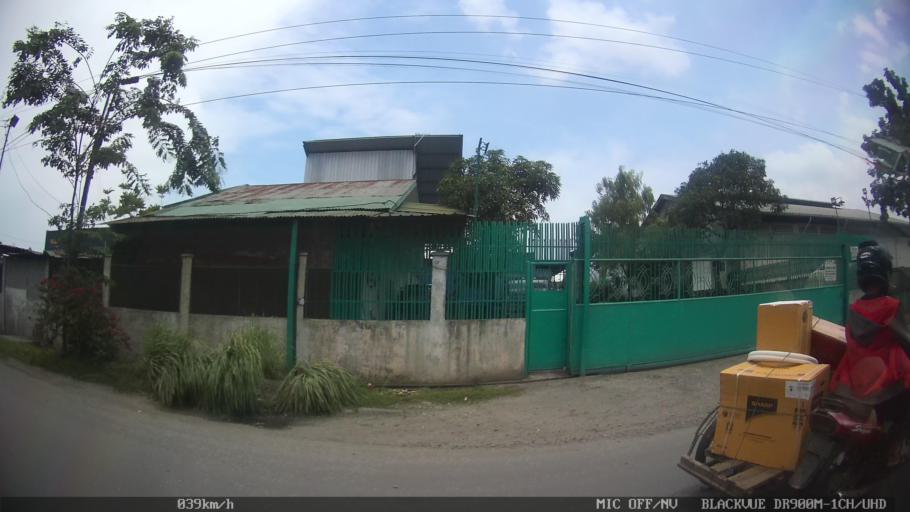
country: ID
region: North Sumatra
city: Labuhan Deli
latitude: 3.6845
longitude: 98.6666
